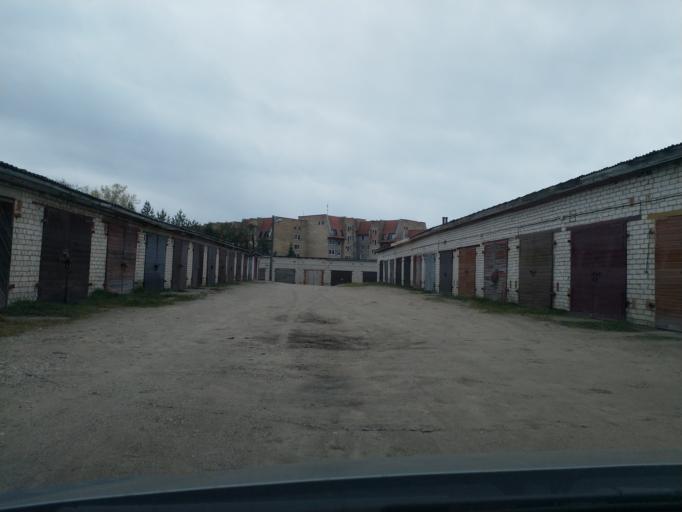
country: LV
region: Kuldigas Rajons
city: Kuldiga
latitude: 56.9790
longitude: 21.9590
